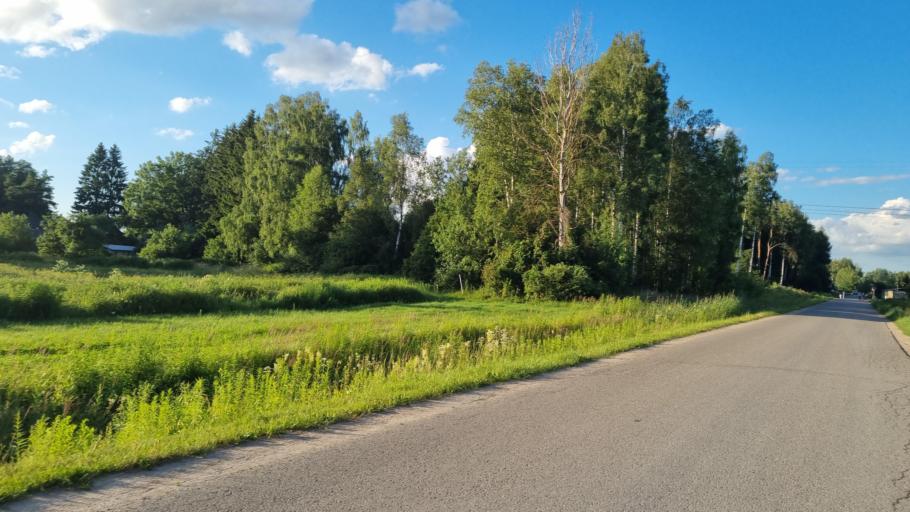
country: LV
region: Kekava
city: Balozi
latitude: 56.8721
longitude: 24.1458
